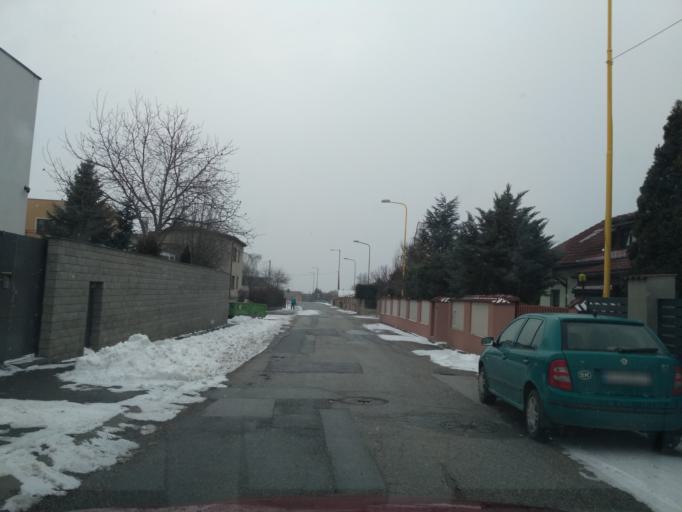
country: SK
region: Kosicky
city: Kosice
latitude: 48.7144
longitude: 21.2219
